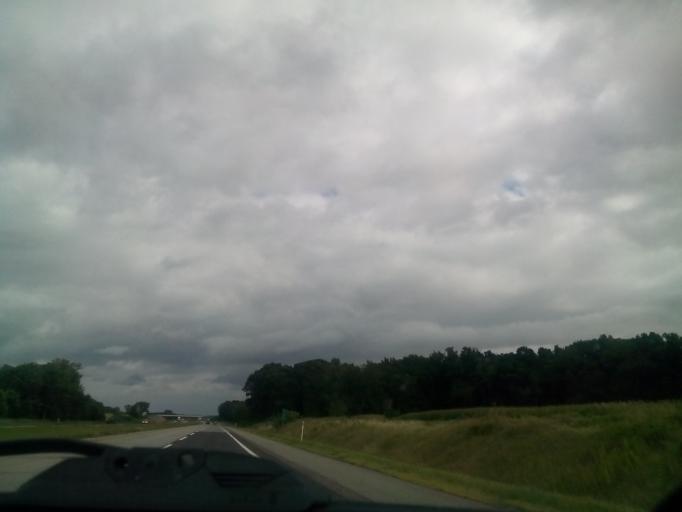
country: US
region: Indiana
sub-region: Steuben County
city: Fremont
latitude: 41.6994
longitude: -84.9162
